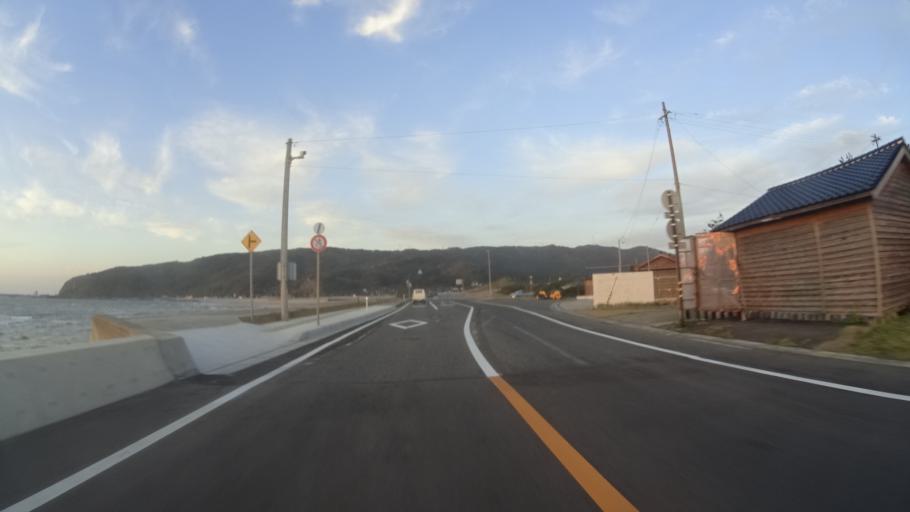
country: JP
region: Ishikawa
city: Nanao
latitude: 37.2843
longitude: 136.7353
